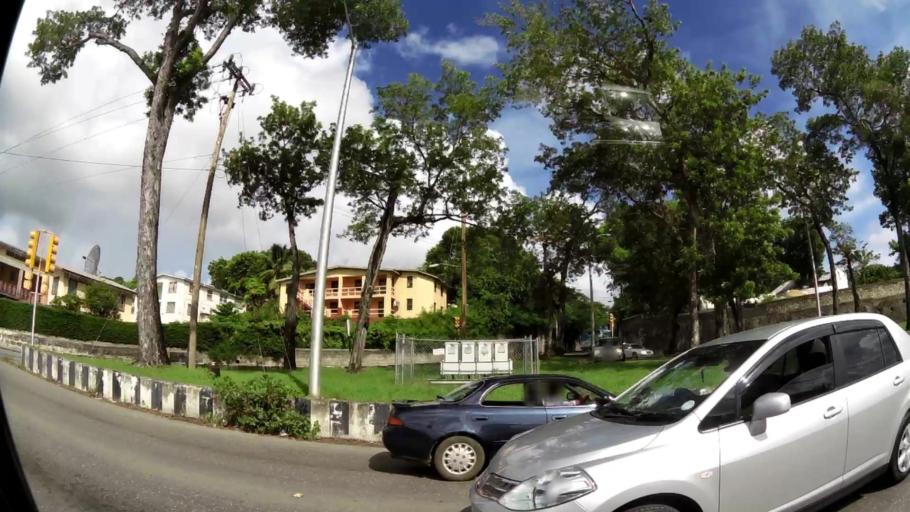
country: BB
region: Saint Michael
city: Bridgetown
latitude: 13.1019
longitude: -59.6014
